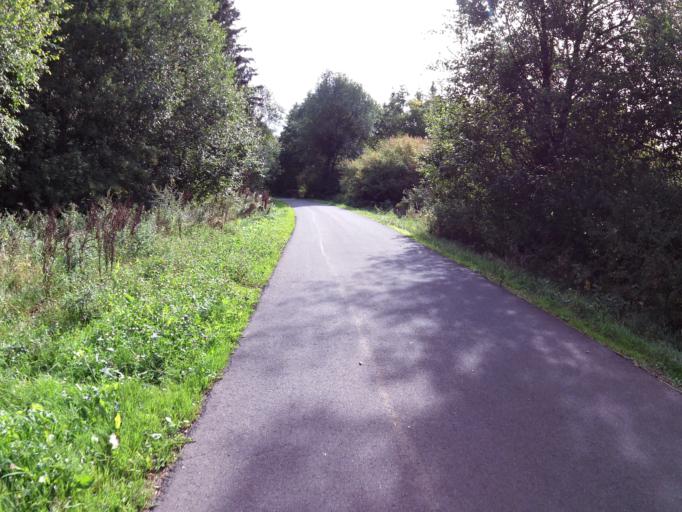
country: DE
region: Rheinland-Pfalz
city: Winterscheid
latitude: 50.2336
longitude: 6.2611
